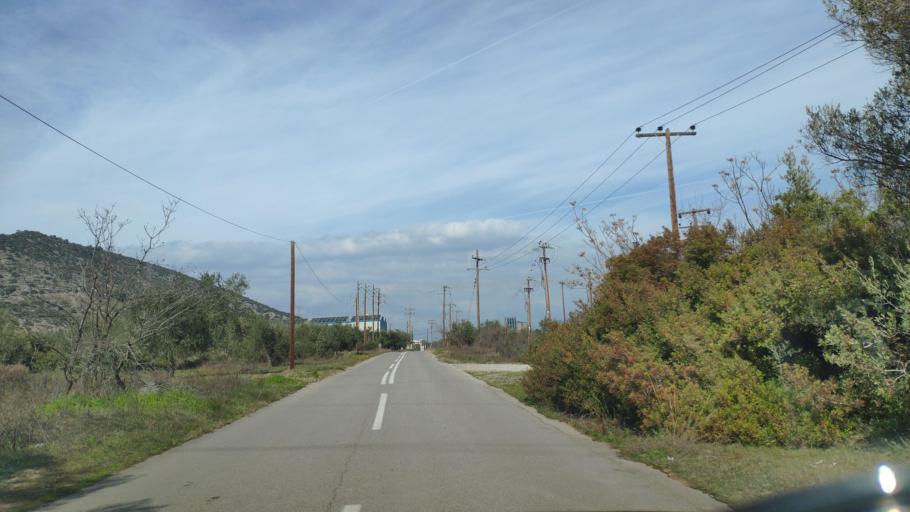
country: GR
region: Central Greece
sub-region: Nomos Evvoias
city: Vathi
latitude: 38.4258
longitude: 23.5911
